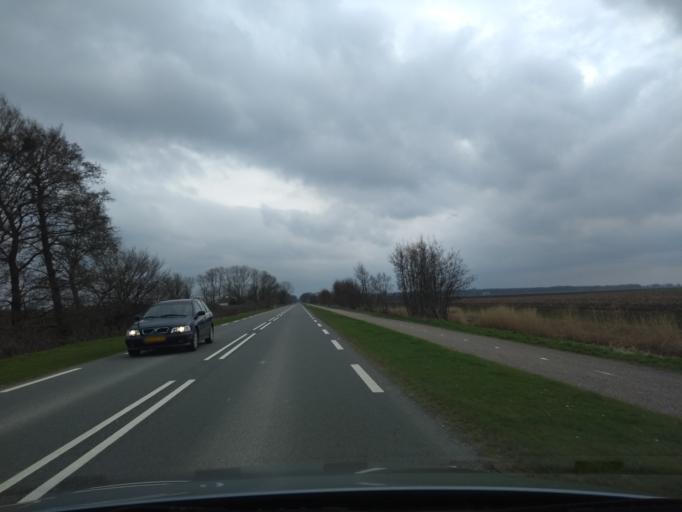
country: NL
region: Overijssel
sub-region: Gemeente Steenwijkerland
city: Blokzijl
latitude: 52.7330
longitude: 5.8606
